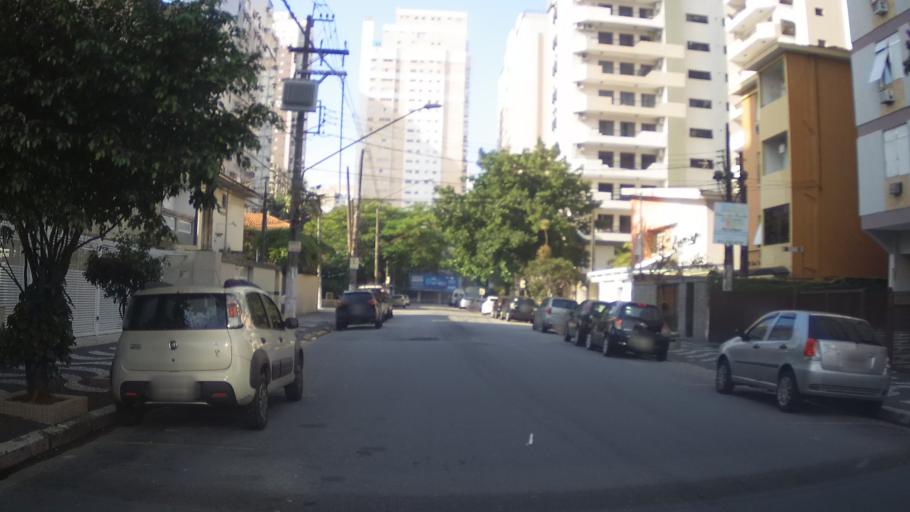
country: BR
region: Sao Paulo
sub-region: Santos
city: Santos
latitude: -23.9634
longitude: -46.3267
